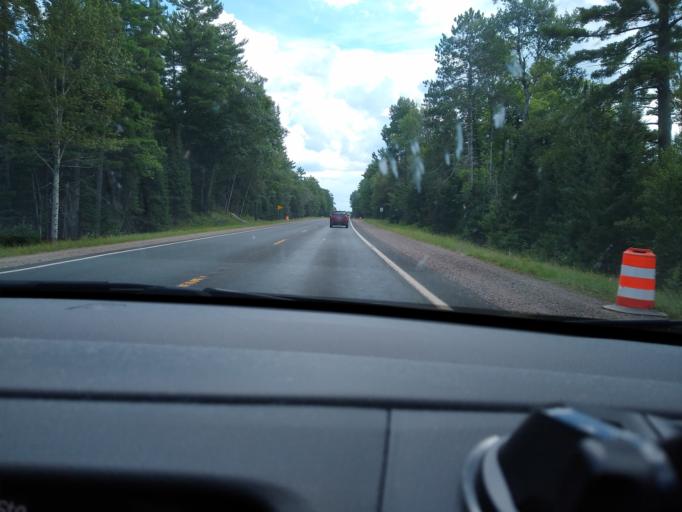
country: US
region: Michigan
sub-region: Iron County
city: Crystal Falls
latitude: 46.2568
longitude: -88.0127
